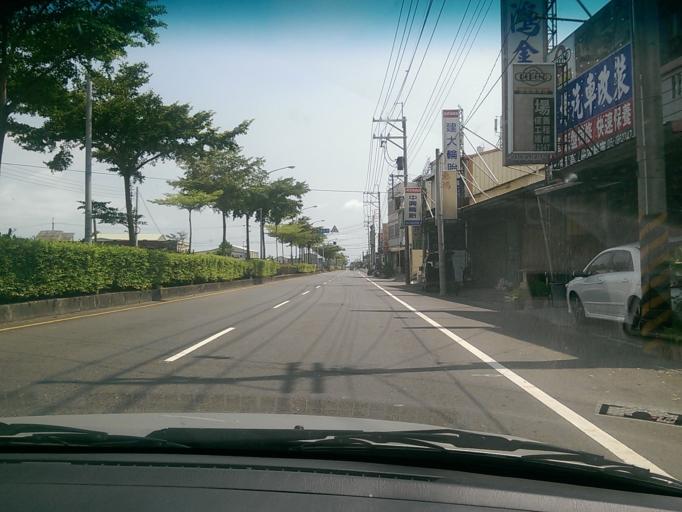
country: TW
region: Taiwan
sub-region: Chiayi
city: Taibao
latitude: 23.6160
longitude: 120.3339
